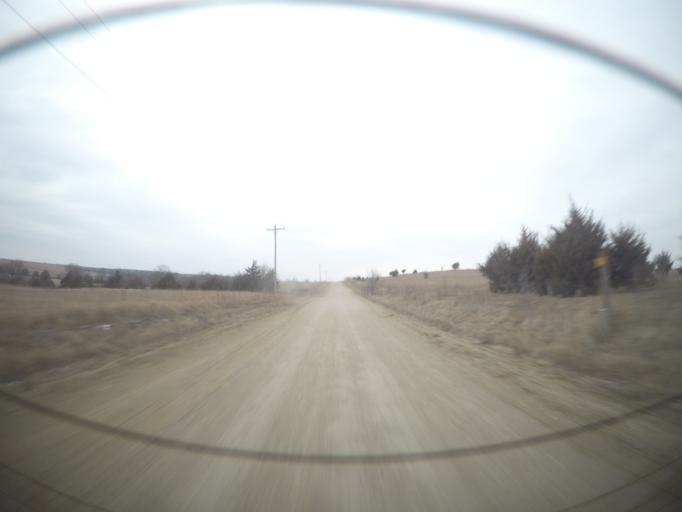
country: US
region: Kansas
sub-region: Pottawatomie County
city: Wamego
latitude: 39.1518
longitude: -96.2713
